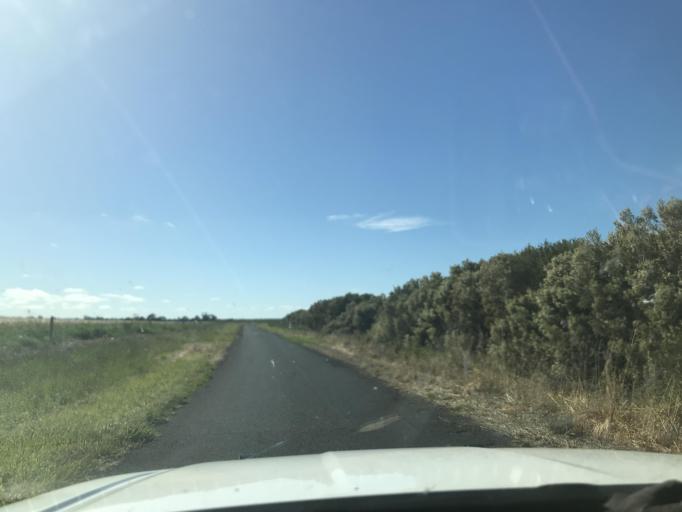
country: AU
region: Victoria
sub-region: Horsham
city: Horsham
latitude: -37.0495
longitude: 141.7447
